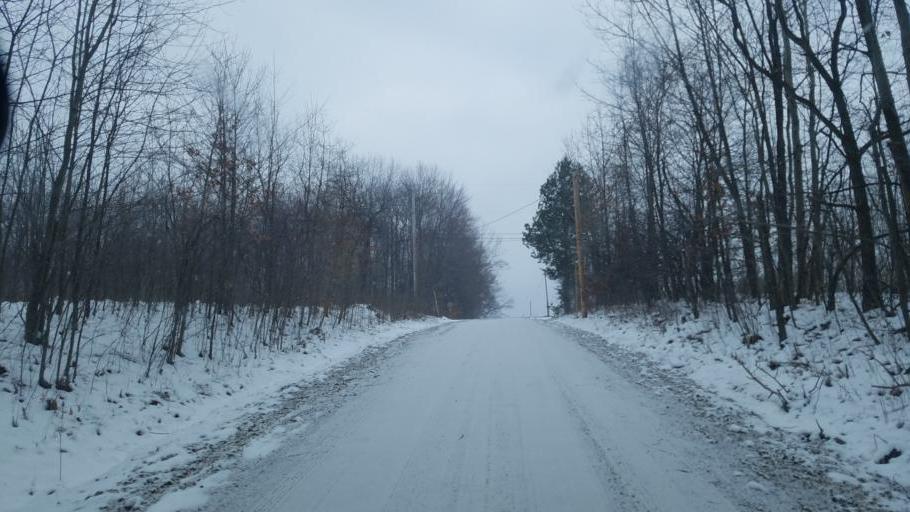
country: US
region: Pennsylvania
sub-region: Mercer County
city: Stoneboro
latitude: 41.4037
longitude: -80.0080
